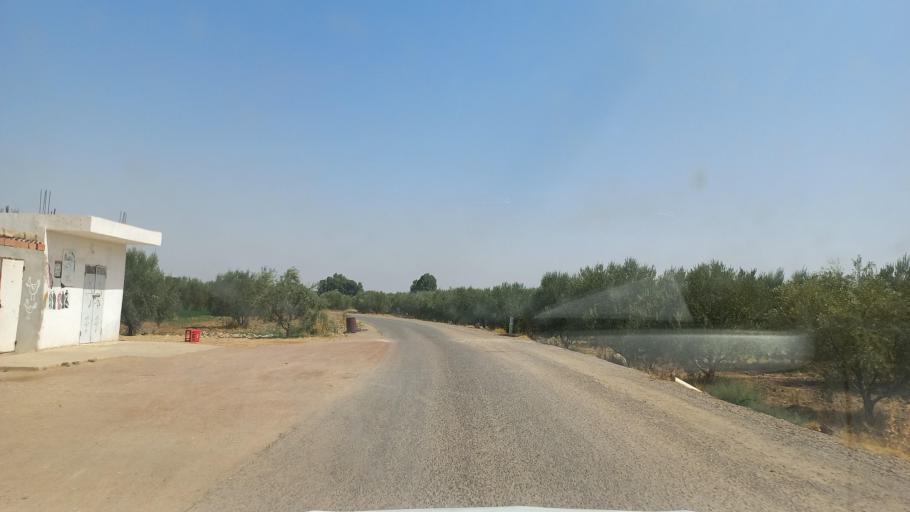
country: TN
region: Al Qasrayn
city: Kasserine
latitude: 35.2363
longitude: 9.0359
